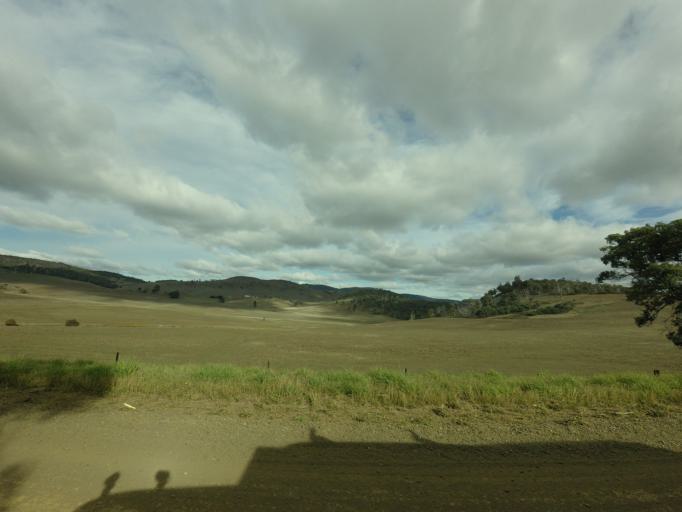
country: AU
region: Tasmania
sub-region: Brighton
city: Bridgewater
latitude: -42.4611
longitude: 147.2732
